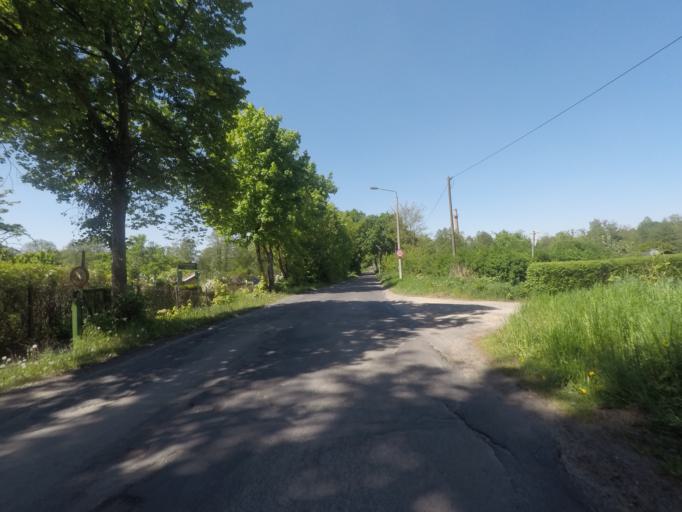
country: DE
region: Brandenburg
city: Melchow
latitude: 52.8479
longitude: 13.7171
